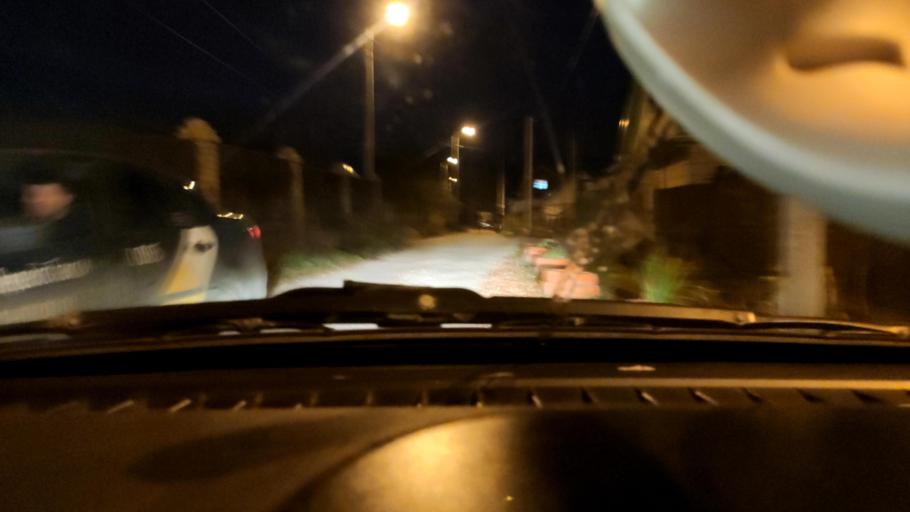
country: RU
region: Perm
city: Froly
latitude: 57.9752
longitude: 56.3027
